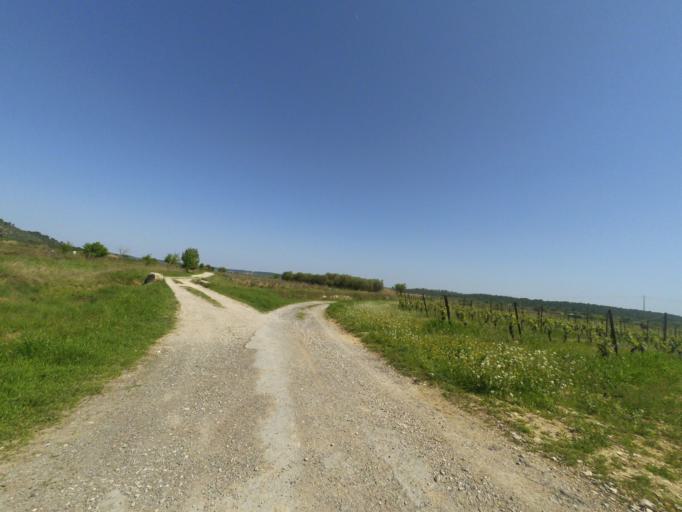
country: FR
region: Languedoc-Roussillon
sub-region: Departement du Gard
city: Congenies
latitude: 43.7741
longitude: 4.1691
